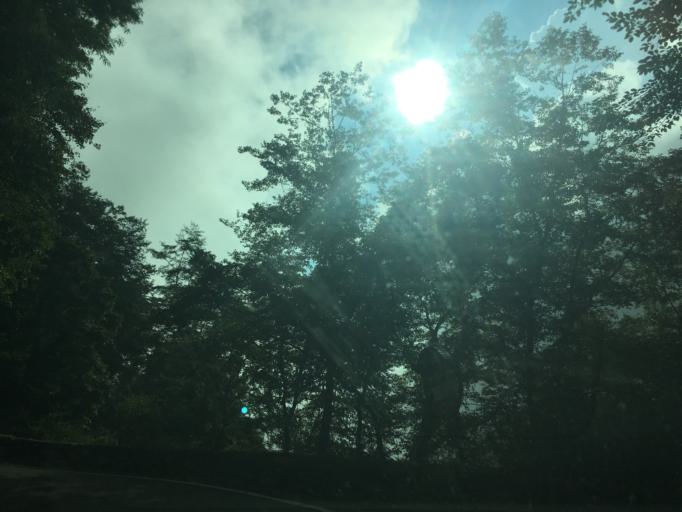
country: TW
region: Taiwan
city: Fengyuan
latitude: 24.2326
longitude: 120.9674
